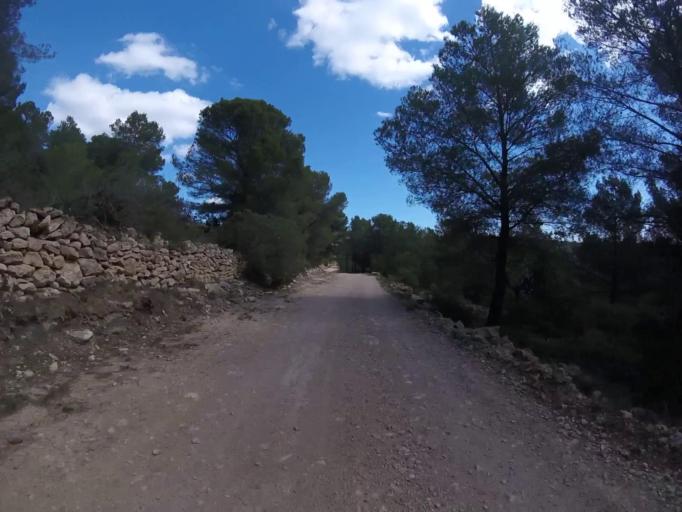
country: ES
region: Valencia
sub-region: Provincia de Castello
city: Santa Magdalena de Pulpis
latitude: 40.3133
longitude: 0.3292
